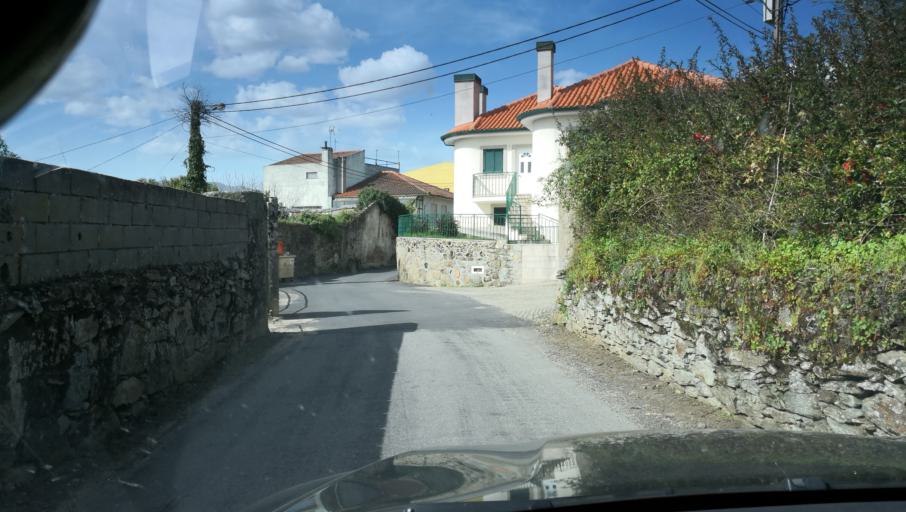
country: PT
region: Vila Real
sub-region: Vila Real
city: Vila Real
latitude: 41.2821
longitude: -7.7334
